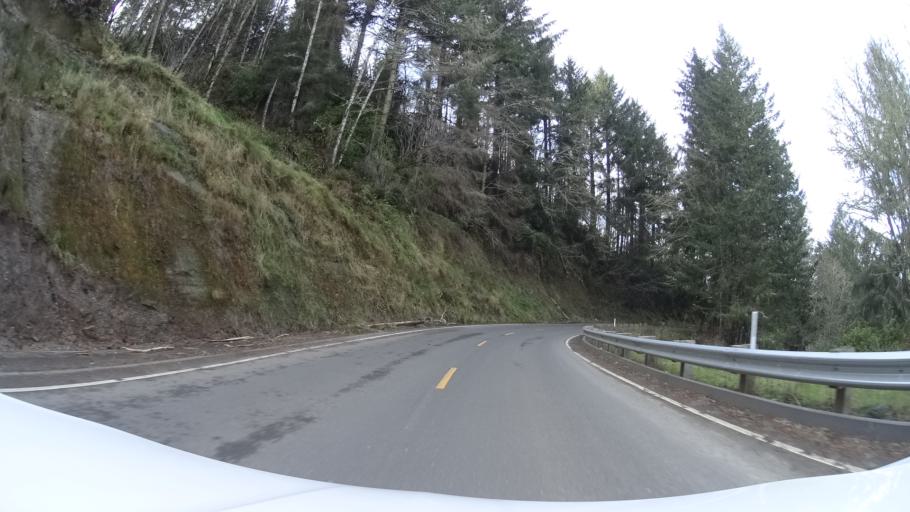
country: US
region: California
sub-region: Humboldt County
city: Ferndale
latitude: 40.5621
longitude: -124.2733
